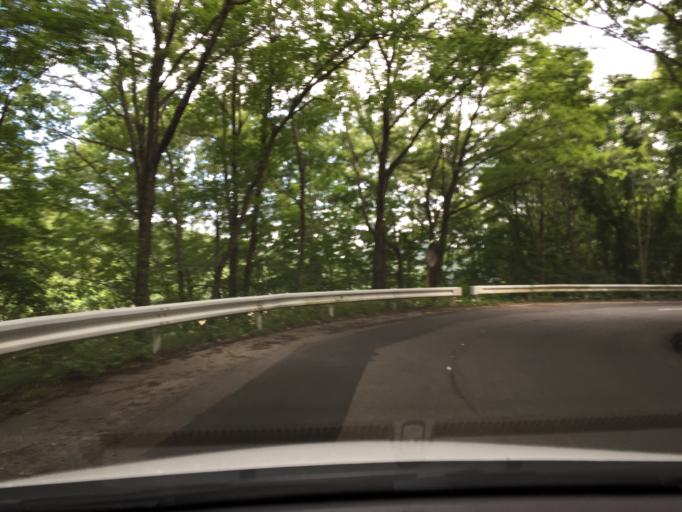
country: JP
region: Tochigi
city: Kuroiso
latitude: 37.2523
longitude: 140.0718
